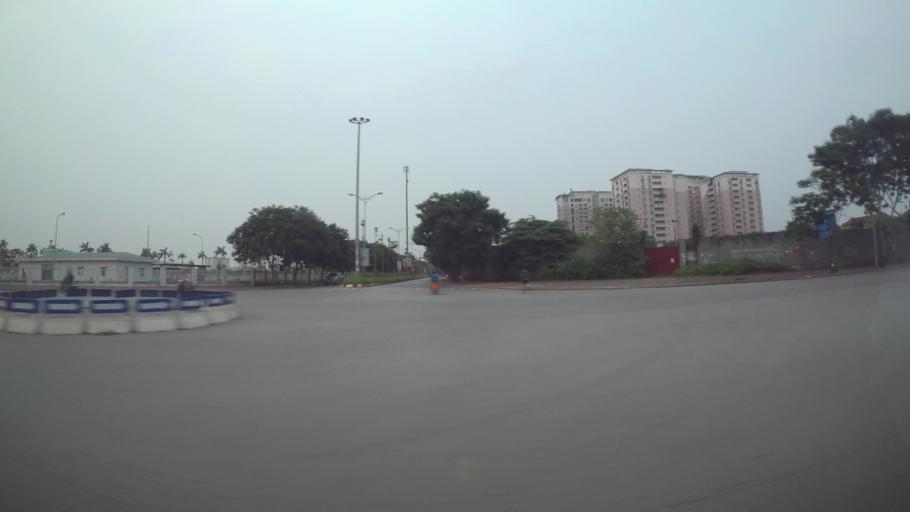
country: VN
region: Ha Noi
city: Trau Quy
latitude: 21.0579
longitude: 105.9038
